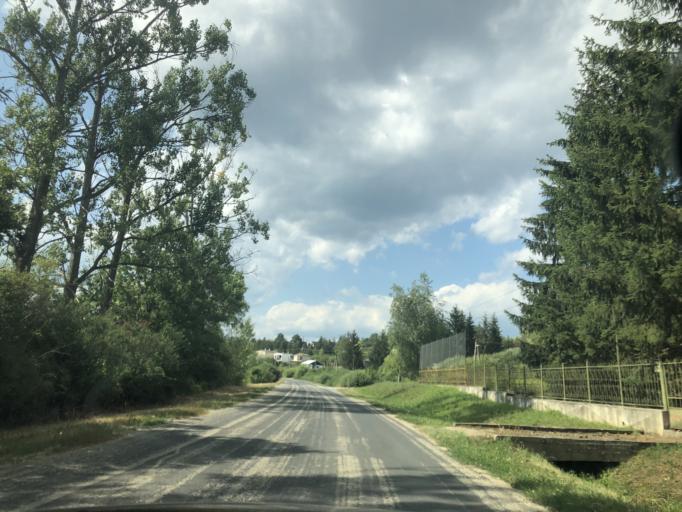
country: HU
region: Borsod-Abauj-Zemplen
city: Szendro
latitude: 48.4545
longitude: 20.7968
